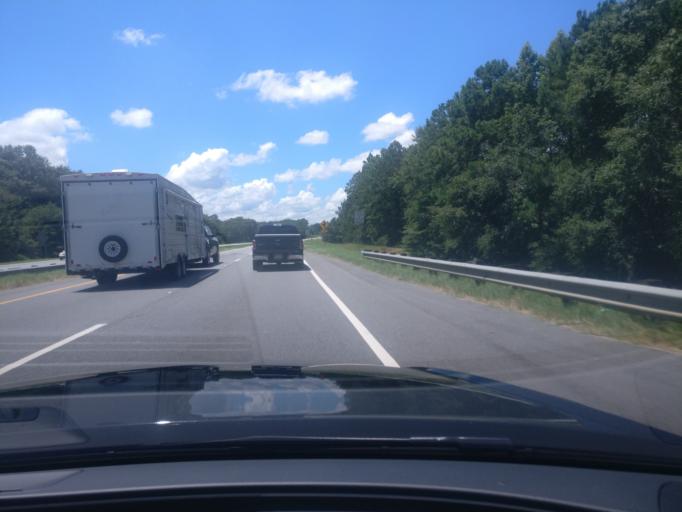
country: US
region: Georgia
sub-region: Tift County
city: Omega
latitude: 31.4741
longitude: -83.6659
